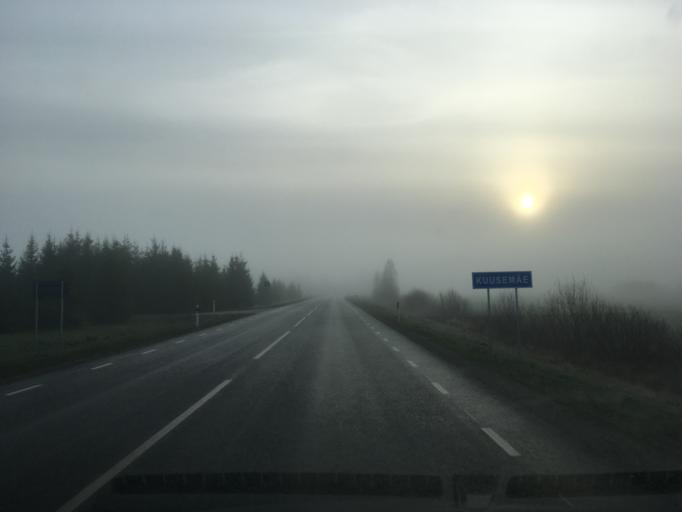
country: EE
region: Harju
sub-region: Anija vald
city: Kehra
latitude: 59.3757
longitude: 25.3097
